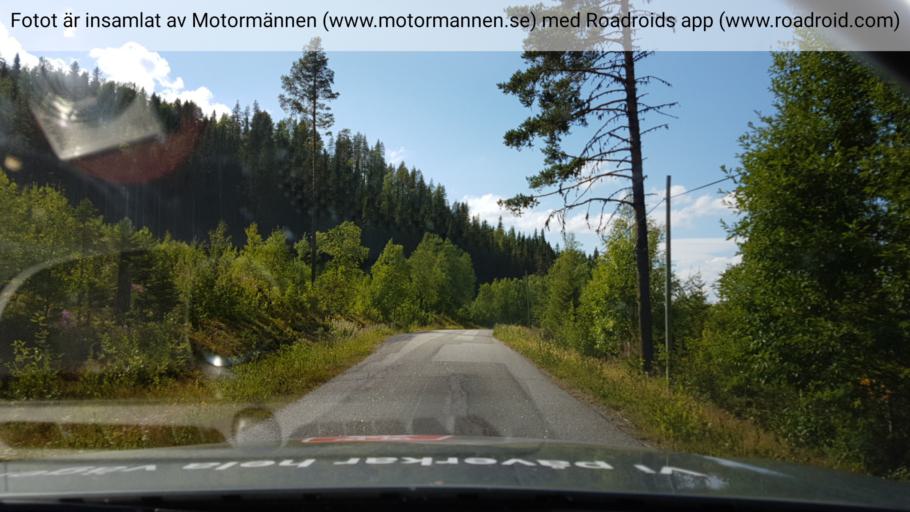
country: SE
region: Vaesterbotten
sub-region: Dorotea Kommun
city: Dorotea
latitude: 64.1273
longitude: 16.3004
